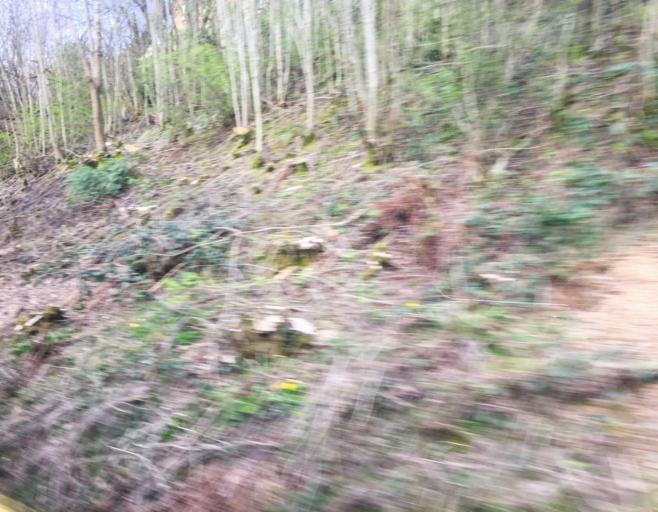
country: GB
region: Scotland
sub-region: West Dunbartonshire
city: Old Kilpatrick
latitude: 55.9217
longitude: -4.4491
